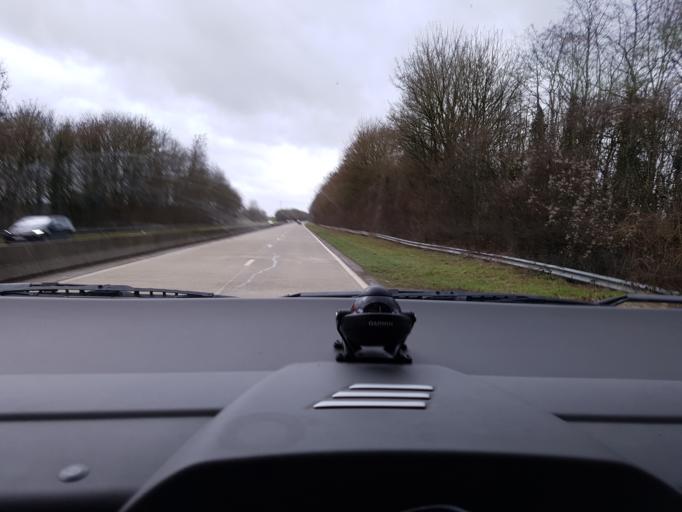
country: BE
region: Wallonia
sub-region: Province de Namur
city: Houyet
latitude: 50.2416
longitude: 4.9872
